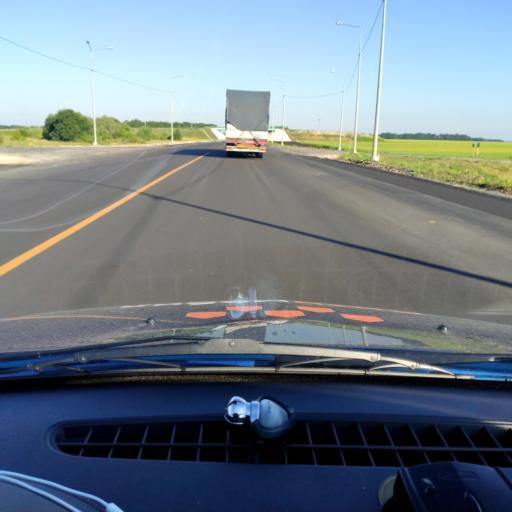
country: RU
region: Orjol
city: Zmiyevka
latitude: 52.6989
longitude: 36.3794
